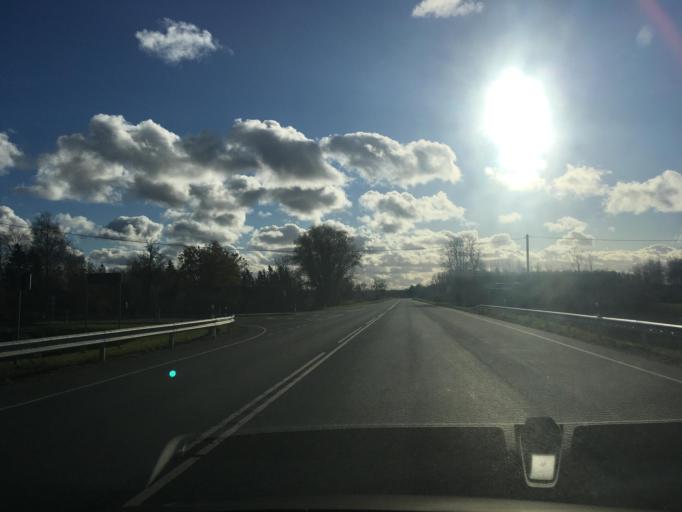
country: EE
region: Harju
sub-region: Nissi vald
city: Turba
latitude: 58.8609
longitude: 24.0743
